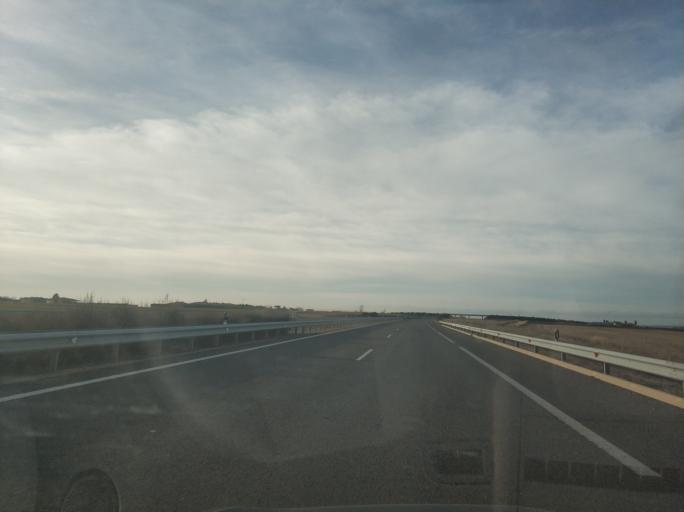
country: ES
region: Castille and Leon
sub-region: Provincia de Salamanca
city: Castellanos de Villiquera
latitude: 41.0553
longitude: -5.6755
